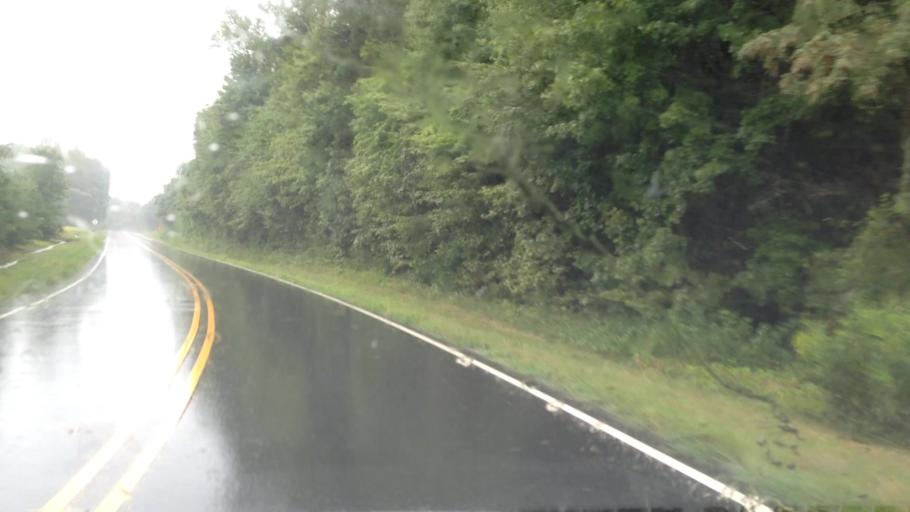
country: US
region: North Carolina
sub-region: Stokes County
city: Danbury
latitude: 36.4320
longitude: -80.1015
